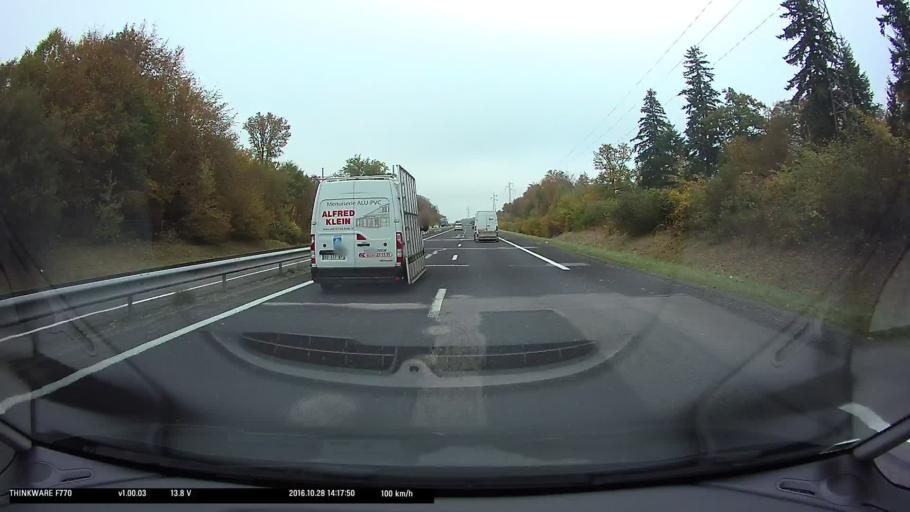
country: FR
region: Lorraine
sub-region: Departement de Meurthe-et-Moselle
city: Chanteheux
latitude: 48.5747
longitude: 6.5546
